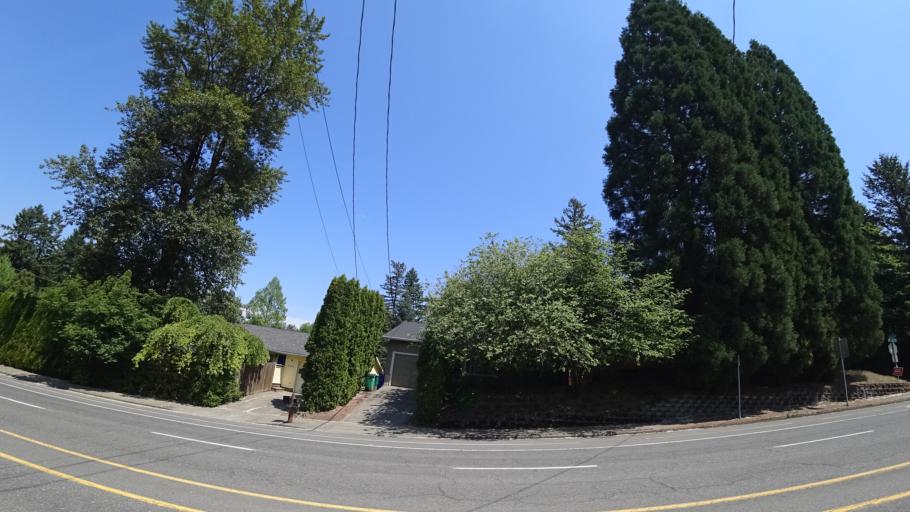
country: US
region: Oregon
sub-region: Washington County
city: Metzger
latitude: 45.4414
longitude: -122.7271
